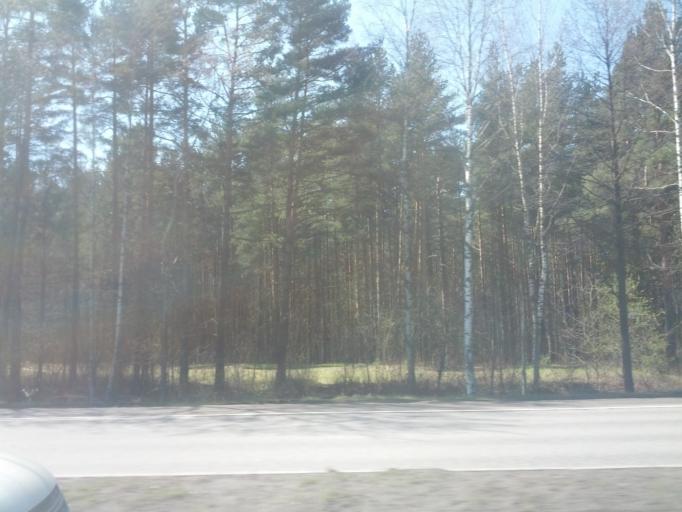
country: RU
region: St.-Petersburg
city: Tarkhovka
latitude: 60.0712
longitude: 29.9689
